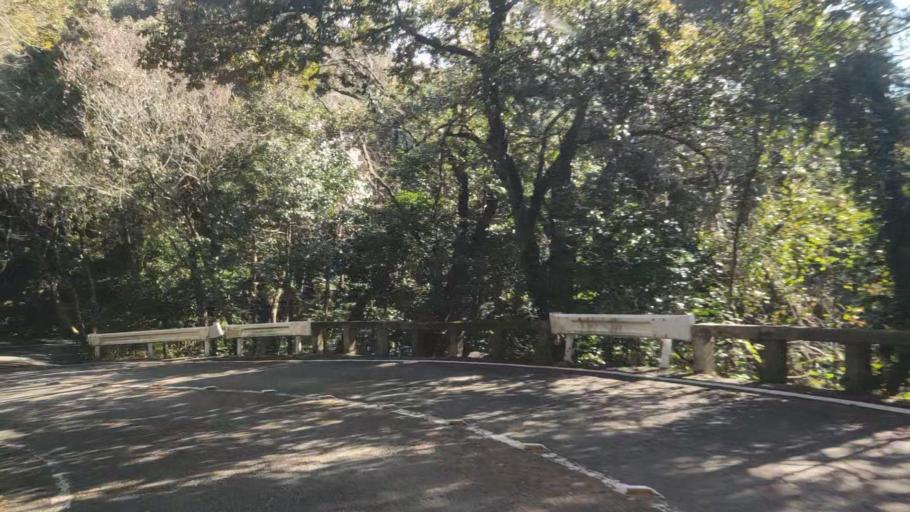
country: JP
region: Gifu
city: Gifu-shi
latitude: 35.4279
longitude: 136.7804
